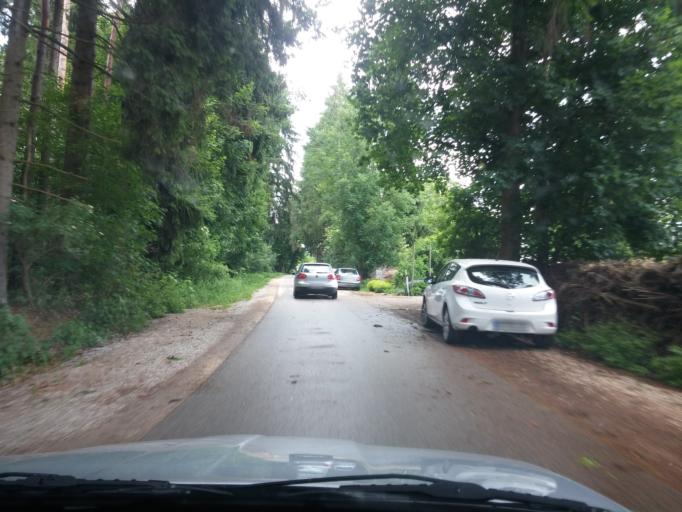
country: DE
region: Bavaria
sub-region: Swabia
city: Illertissen
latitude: 48.2392
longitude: 10.1294
